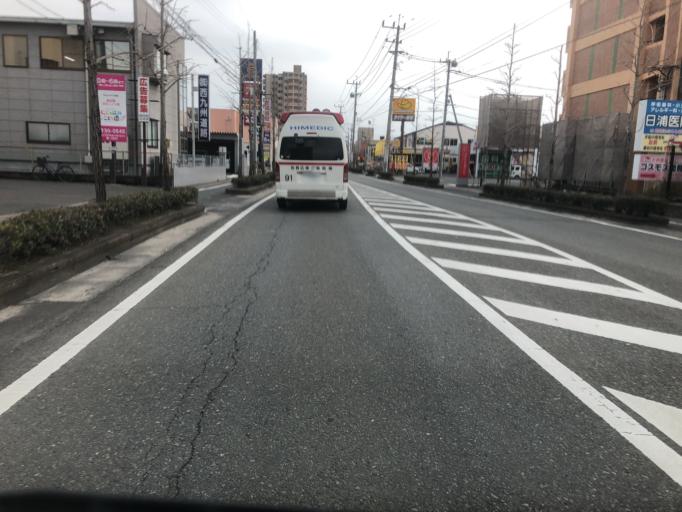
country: JP
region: Saga Prefecture
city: Saga-shi
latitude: 33.2773
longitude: 130.2703
